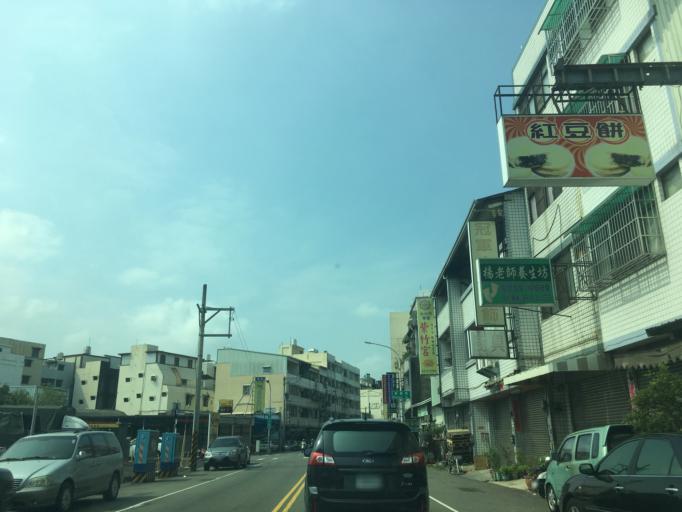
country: TW
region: Taiwan
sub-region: Taichung City
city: Taichung
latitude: 24.1329
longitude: 120.7056
